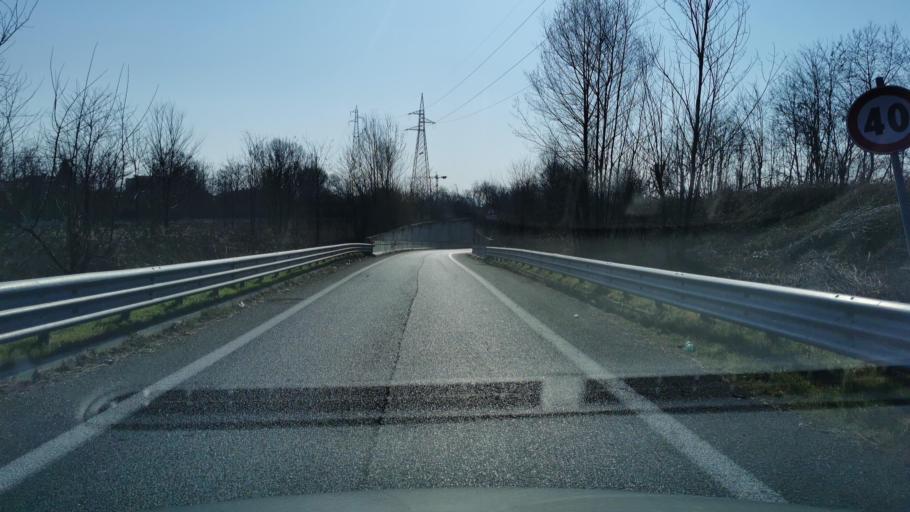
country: IT
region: Piedmont
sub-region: Provincia di Torino
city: Borgaro Torinese
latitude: 45.1458
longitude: 7.6480
